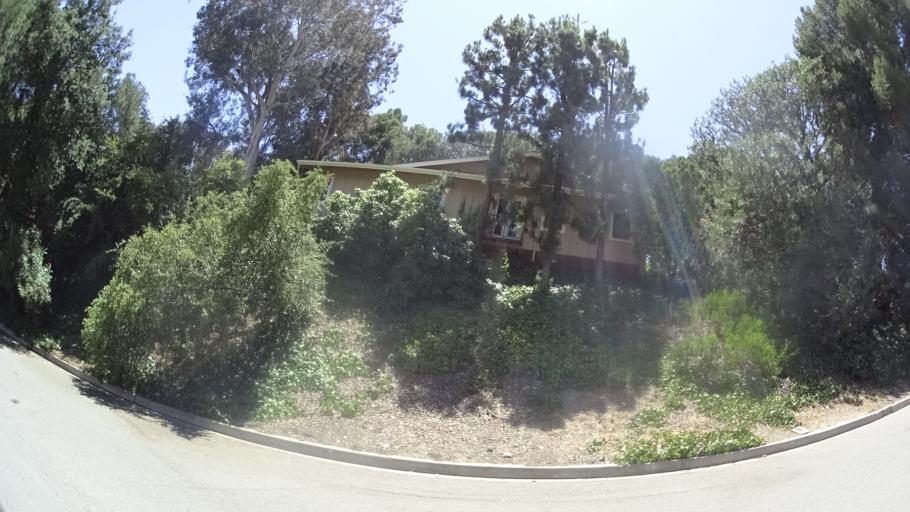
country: US
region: California
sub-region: Los Angeles County
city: Sherman Oaks
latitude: 34.1382
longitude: -118.4731
